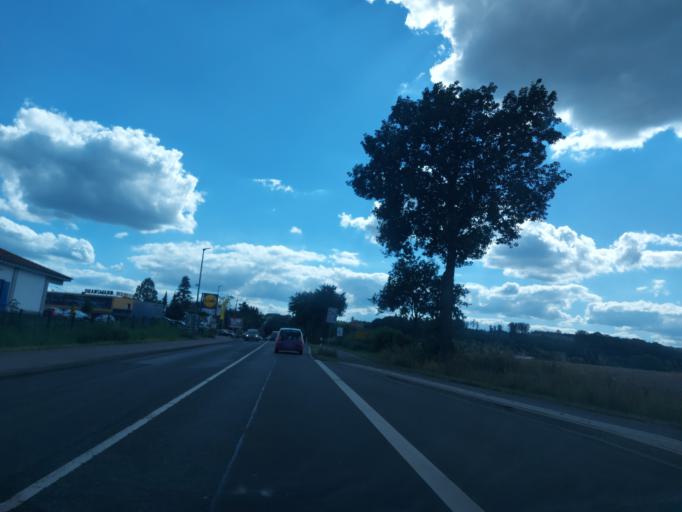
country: DE
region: Lower Saxony
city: Georgsmarienhutte
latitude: 52.2274
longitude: 8.0128
